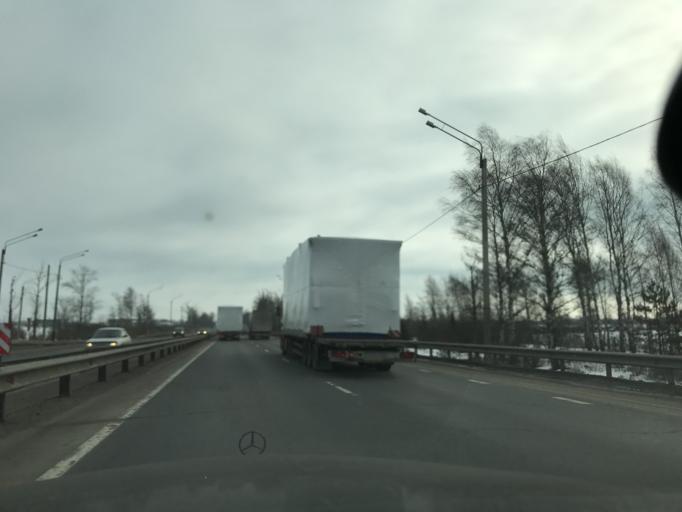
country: RU
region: Vladimir
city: Luknovo
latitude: 56.2394
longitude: 42.0760
